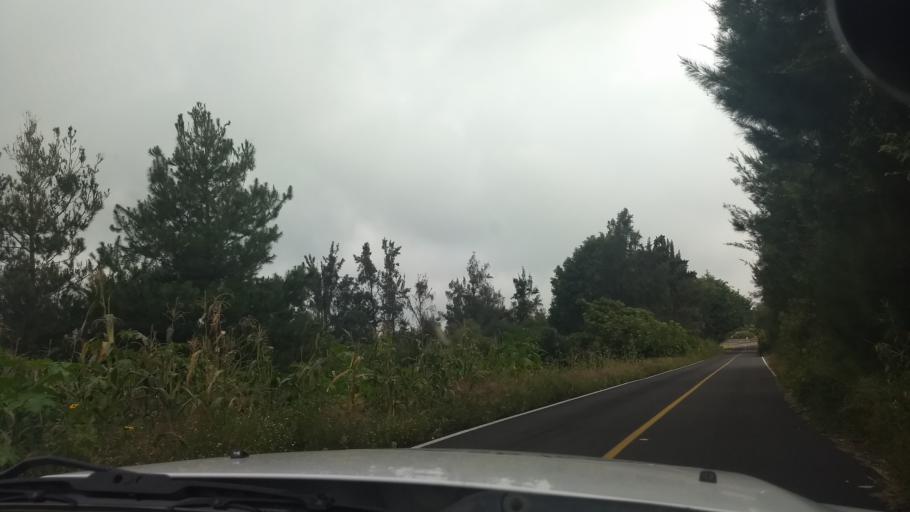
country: MX
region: Colima
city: Queseria
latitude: 19.3999
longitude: -103.6154
